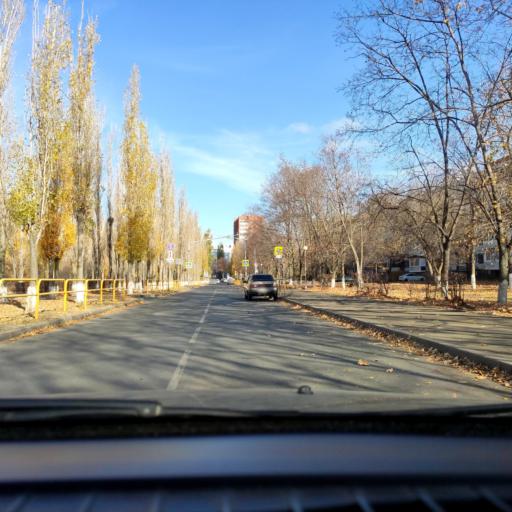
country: RU
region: Samara
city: Tol'yatti
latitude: 53.5218
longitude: 49.2853
